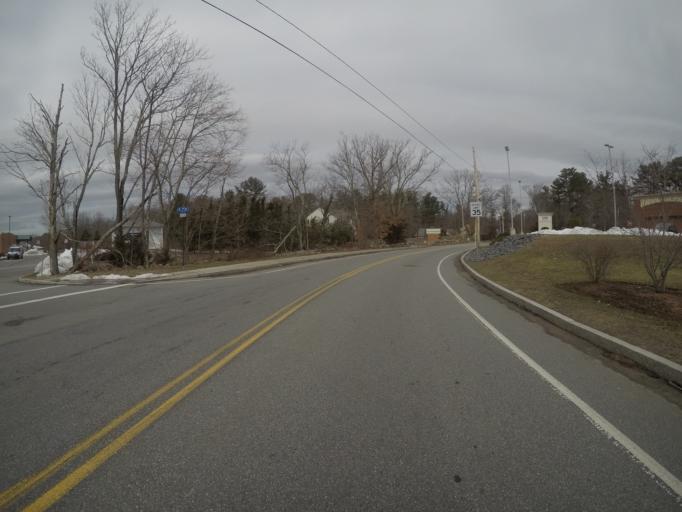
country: US
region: Massachusetts
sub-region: Bristol County
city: Easton
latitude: 42.0243
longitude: -71.1198
